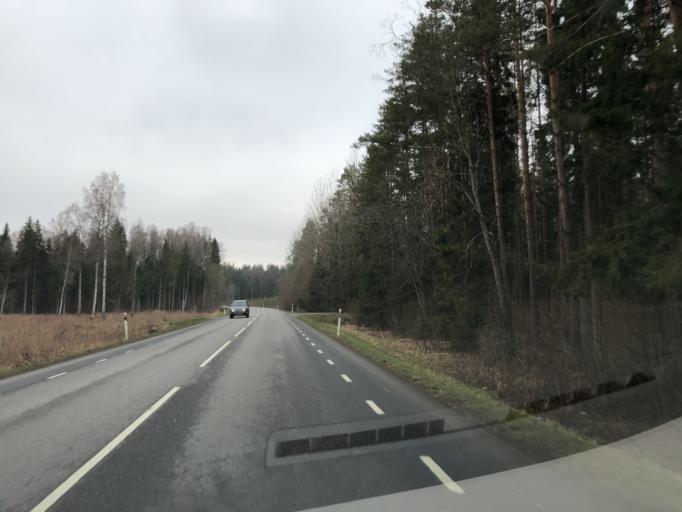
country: EE
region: Laeaene-Virumaa
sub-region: Vaeike-Maarja vald
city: Vaike-Maarja
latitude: 59.0835
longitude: 26.2387
